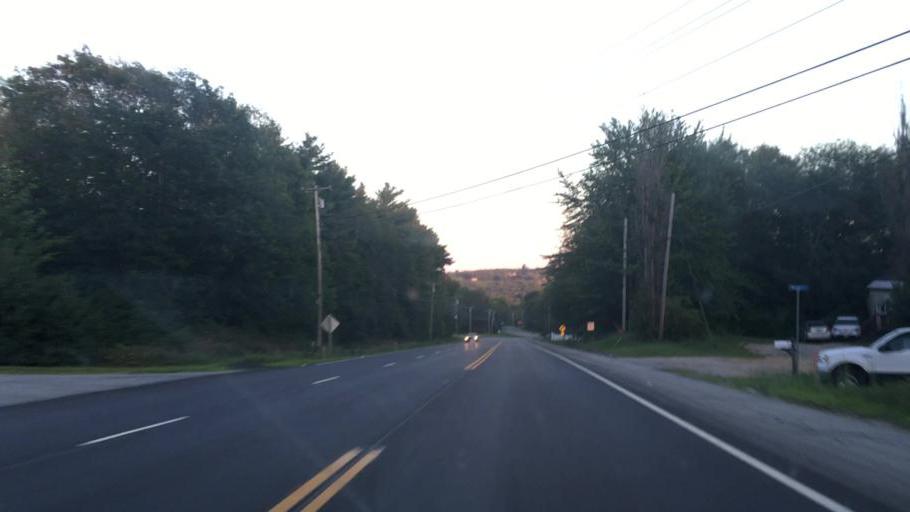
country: US
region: Maine
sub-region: Androscoggin County
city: Turner
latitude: 44.2623
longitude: -70.2626
